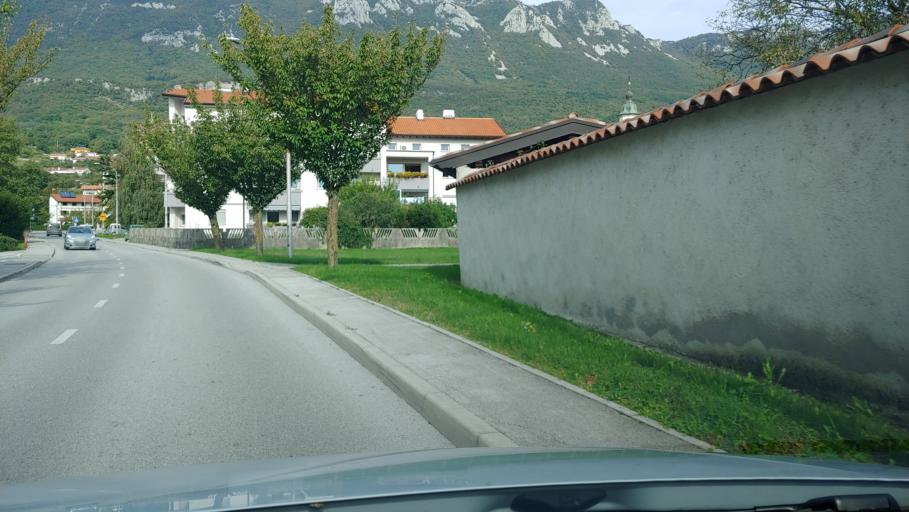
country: SI
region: Ajdovscina
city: Ajdovscina
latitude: 45.8875
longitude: 13.9075
